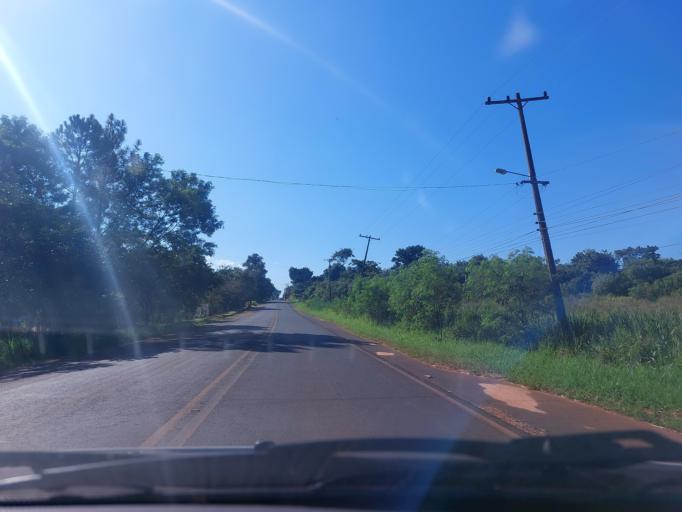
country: PY
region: San Pedro
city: Guayaybi
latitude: -24.5311
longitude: -56.4115
